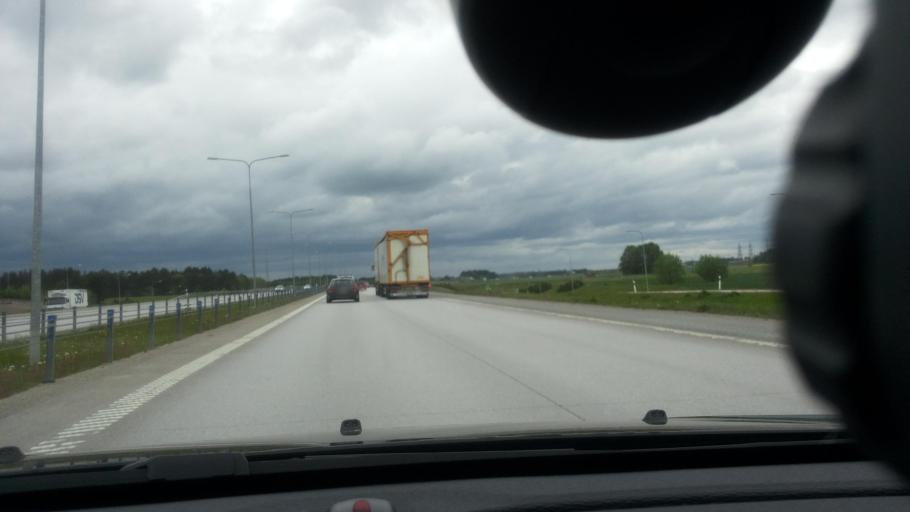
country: SE
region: Uppsala
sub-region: Uppsala Kommun
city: Gamla Uppsala
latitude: 59.8861
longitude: 17.6753
